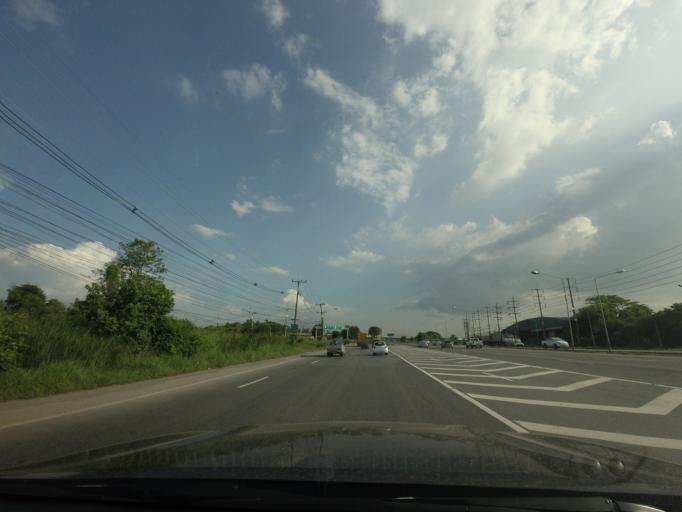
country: TH
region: Sara Buri
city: Saraburi
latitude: 14.5676
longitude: 100.9038
